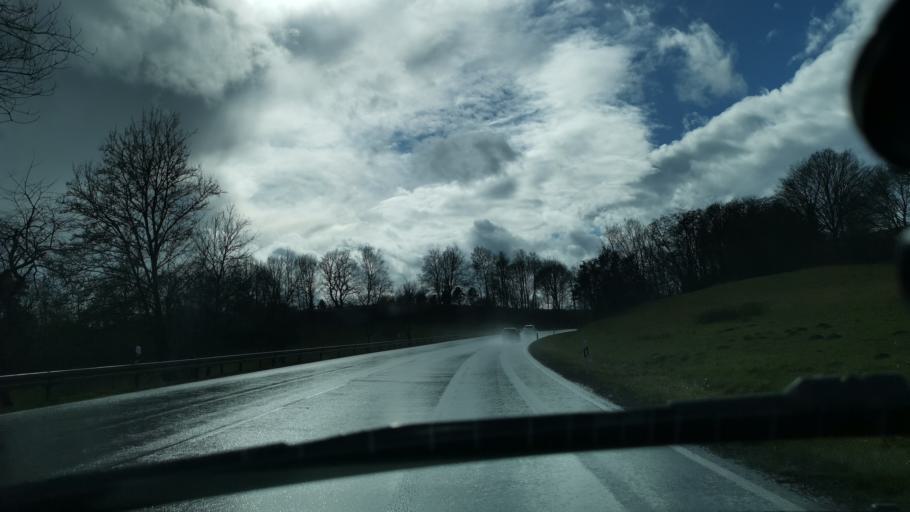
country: DE
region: Hesse
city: Bebra
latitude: 50.9831
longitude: 9.8025
